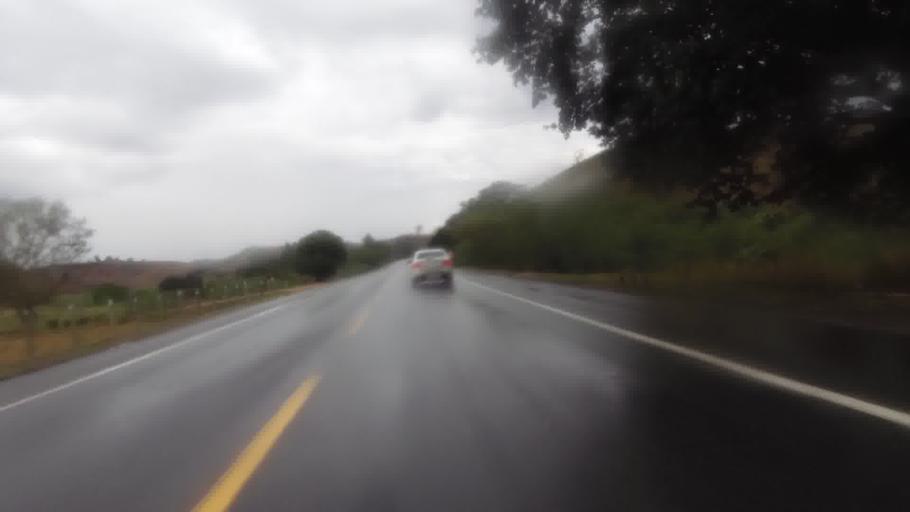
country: BR
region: Espirito Santo
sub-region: Cachoeiro De Itapemirim
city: Cachoeiro de Itapemirim
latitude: -21.0042
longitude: -41.1351
